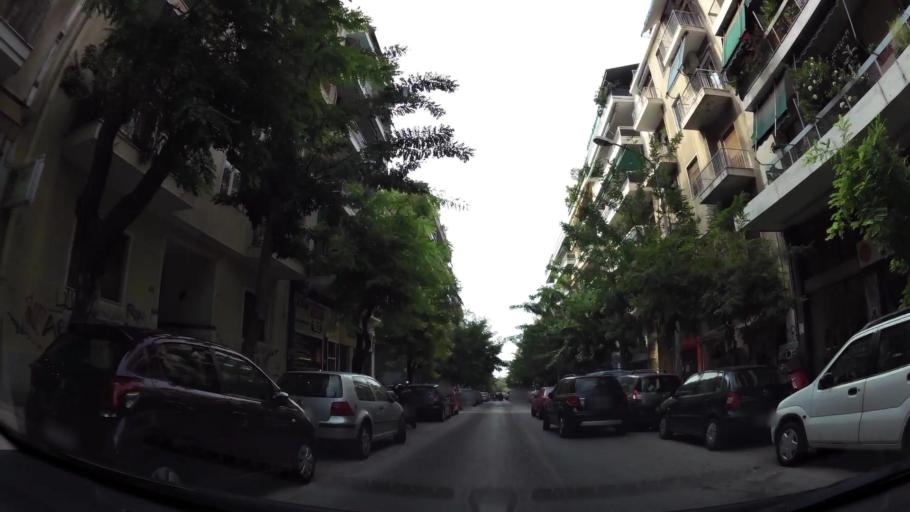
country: GR
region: Attica
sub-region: Nomarchia Athinas
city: Kipseli
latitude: 37.9970
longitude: 23.7396
